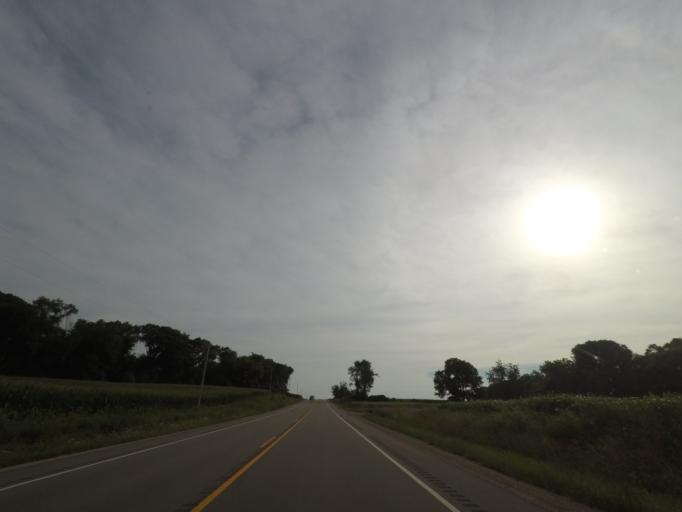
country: US
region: Wisconsin
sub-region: Columbia County
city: Lodi
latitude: 43.3265
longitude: -89.4884
